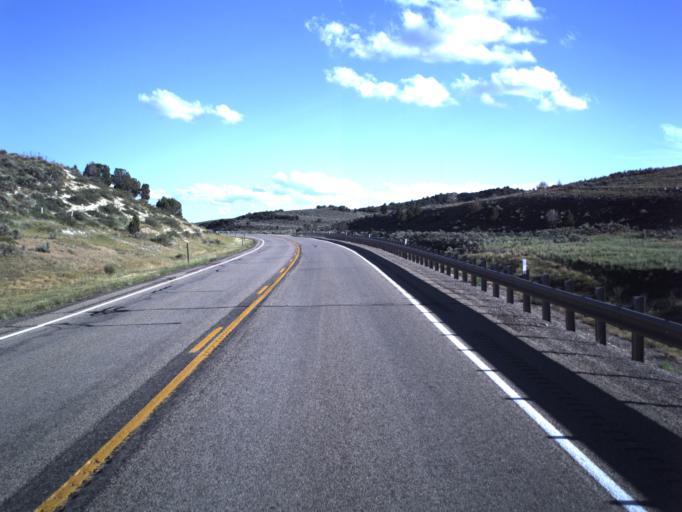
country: US
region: Utah
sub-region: Sanpete County
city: Fairview
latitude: 39.7359
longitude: -111.4771
